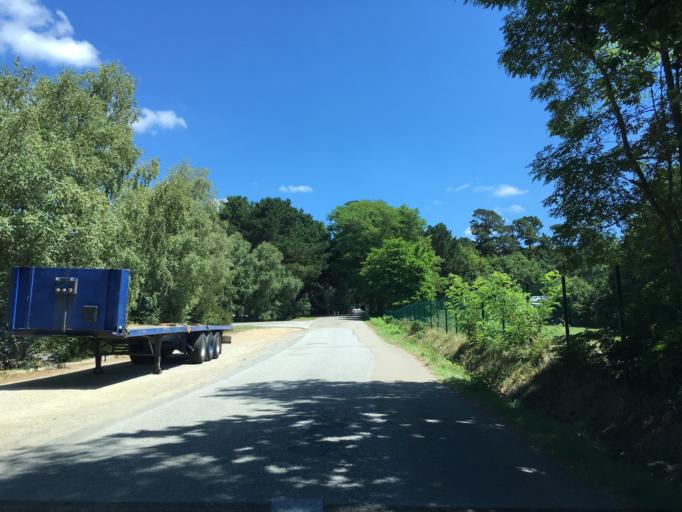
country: FR
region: Brittany
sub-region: Departement du Finistere
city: Quimper
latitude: 47.9739
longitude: -4.0927
